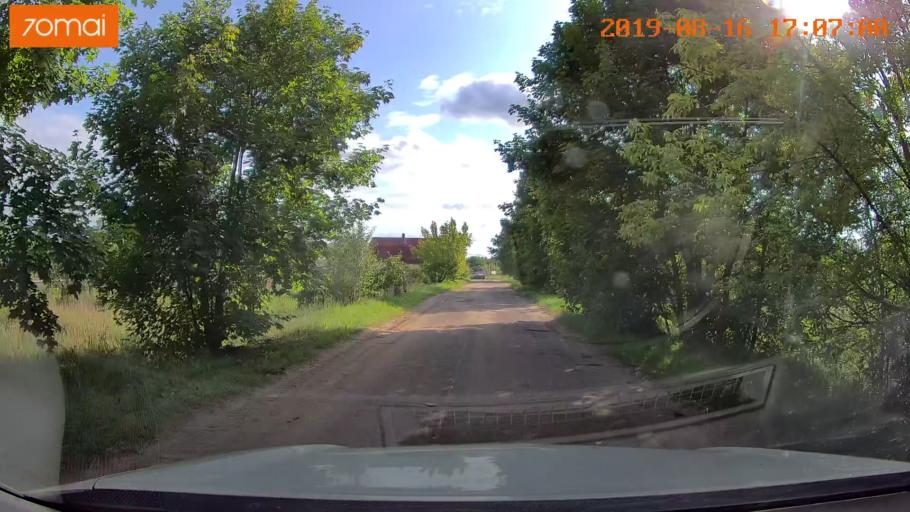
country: BY
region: Mogilev
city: Hlusha
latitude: 53.2215
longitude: 28.9275
